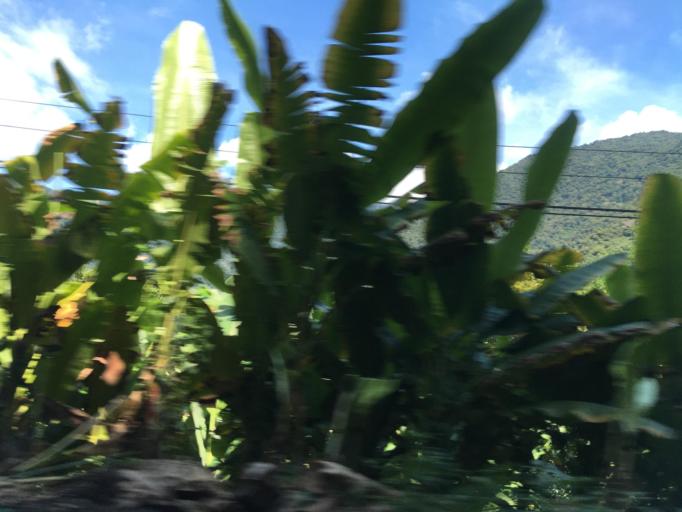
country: TW
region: Taiwan
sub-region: Yilan
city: Yilan
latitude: 24.4380
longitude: 121.7606
